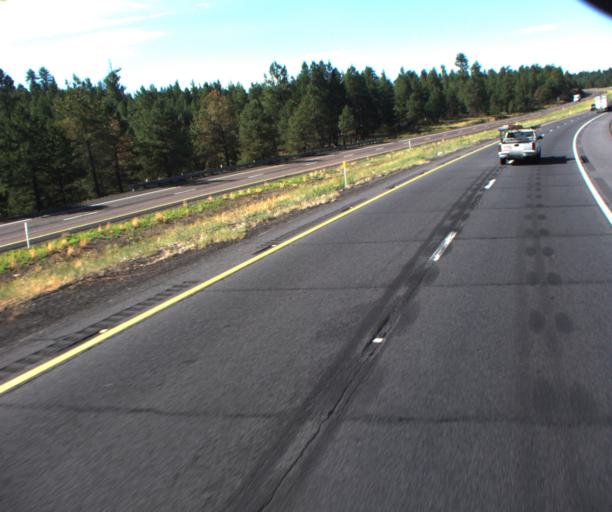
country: US
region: Arizona
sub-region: Coconino County
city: Mountainaire
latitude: 35.0696
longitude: -111.6828
